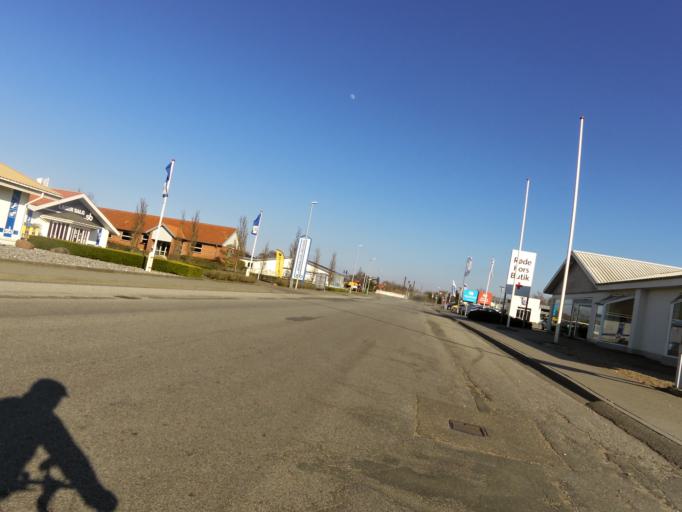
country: DK
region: South Denmark
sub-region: Esbjerg Kommune
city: Ribe
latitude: 55.3454
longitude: 8.7749
